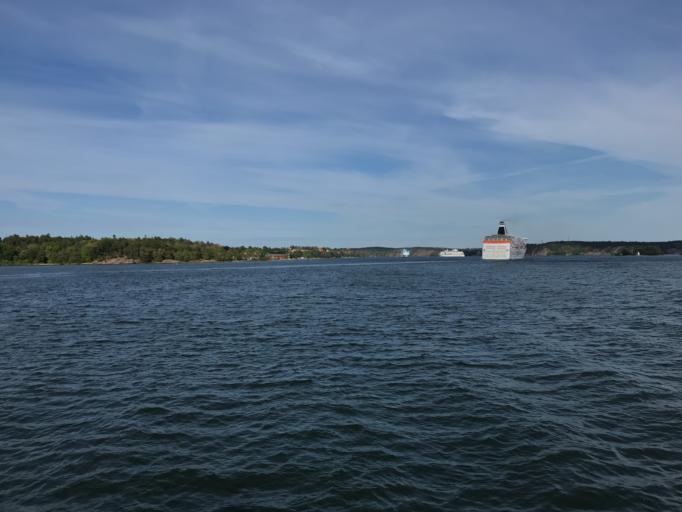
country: SE
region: Stockholm
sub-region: Nacka Kommun
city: Nacka
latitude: 59.3367
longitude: 18.1535
